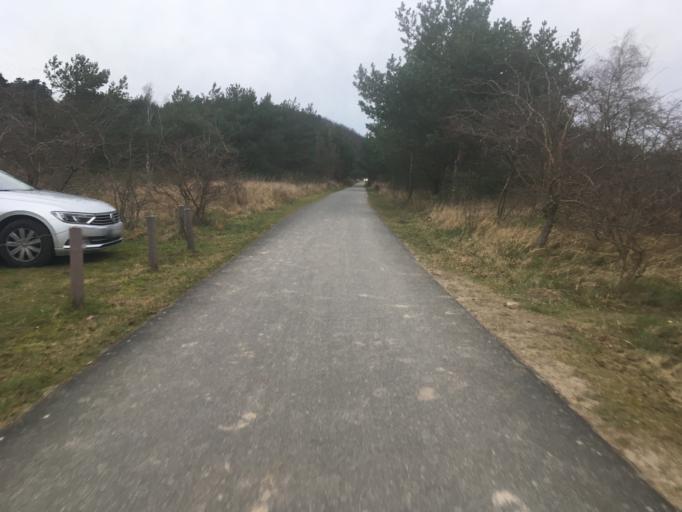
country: DE
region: Mecklenburg-Vorpommern
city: Sagard
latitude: 54.4752
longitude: 13.5717
